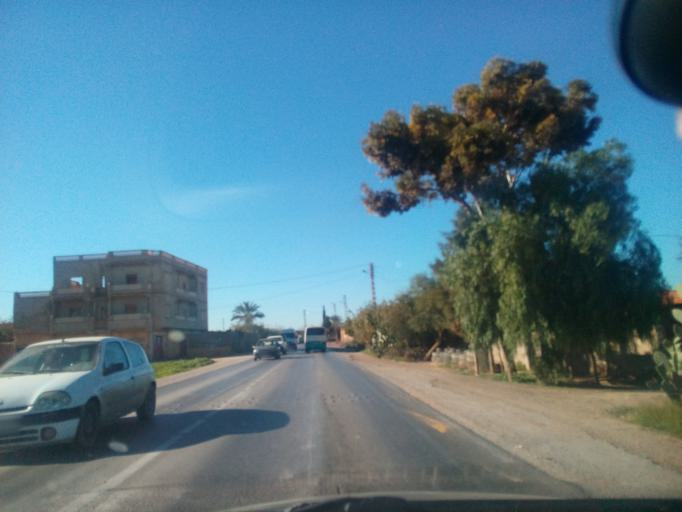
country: DZ
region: Relizane
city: Djidiouia
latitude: 35.8931
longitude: 0.7243
